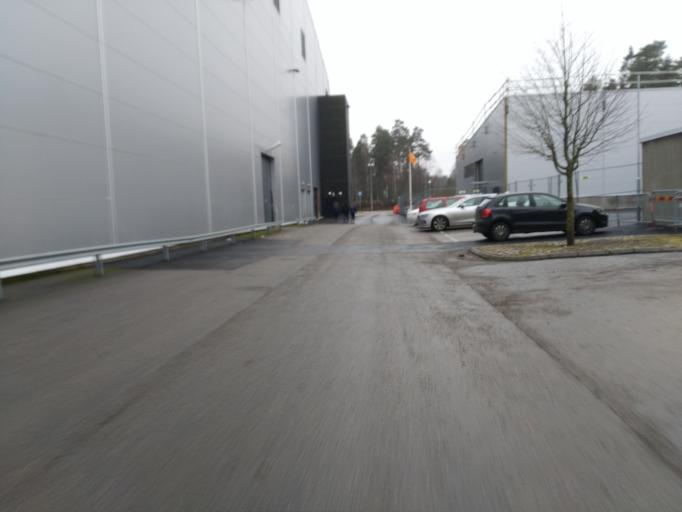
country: SE
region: Vaestra Goetaland
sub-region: Lidkopings Kommun
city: Lidkoping
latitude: 58.4949
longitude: 13.1420
